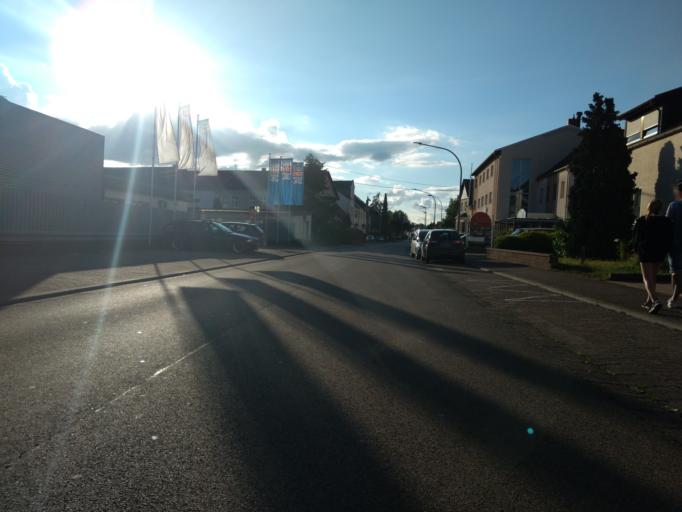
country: DE
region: Saarland
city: Saarlouis
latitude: 49.3275
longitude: 6.7627
